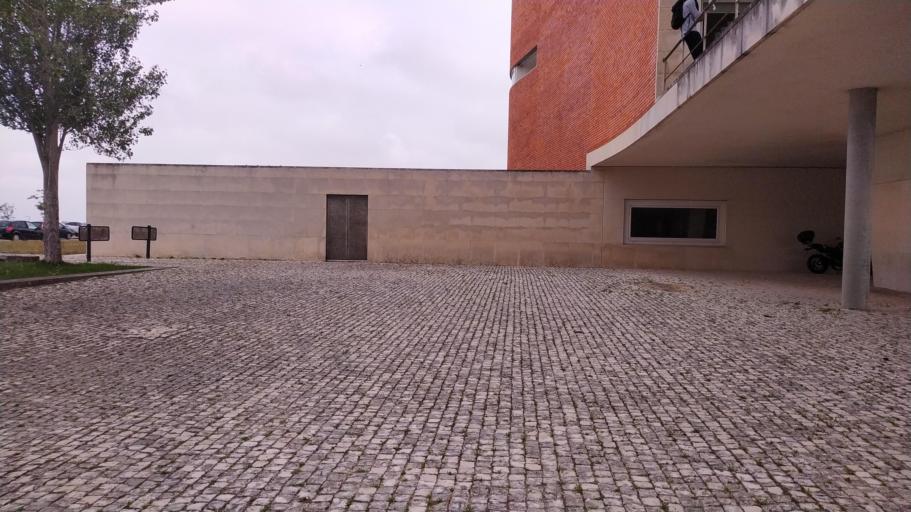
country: PT
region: Aveiro
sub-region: Aveiro
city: Aveiro
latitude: 40.6308
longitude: -8.6596
